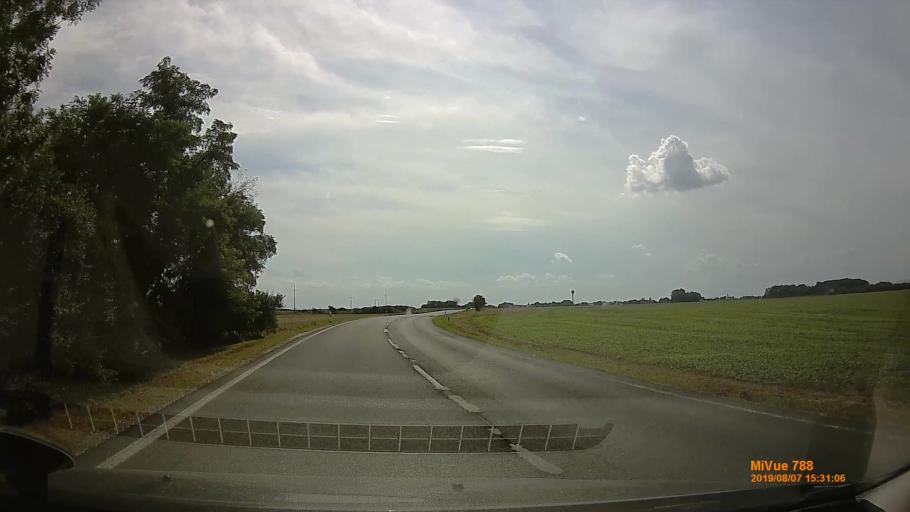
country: HU
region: Vas
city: Vep
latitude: 47.2720
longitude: 16.7554
